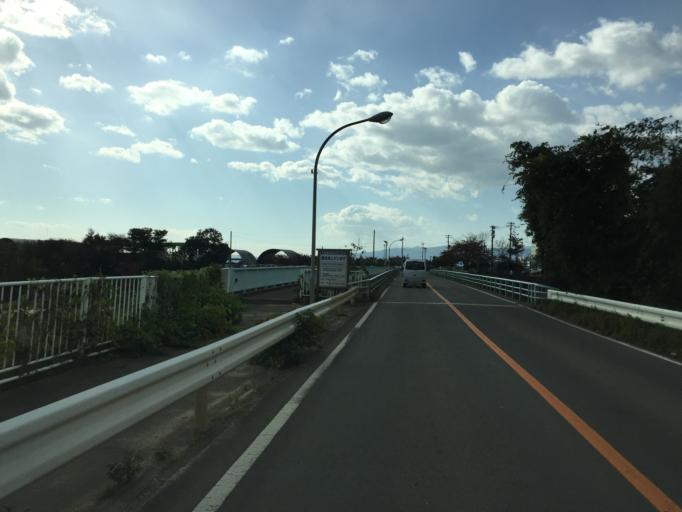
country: JP
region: Fukushima
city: Fukushima-shi
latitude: 37.7855
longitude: 140.3940
